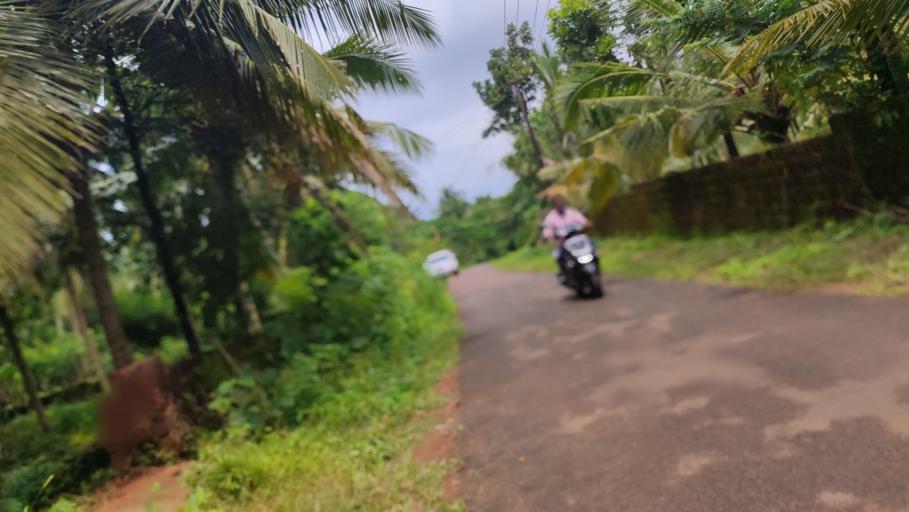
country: IN
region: Kerala
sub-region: Kasaragod District
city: Kannangad
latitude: 12.4011
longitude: 75.0552
